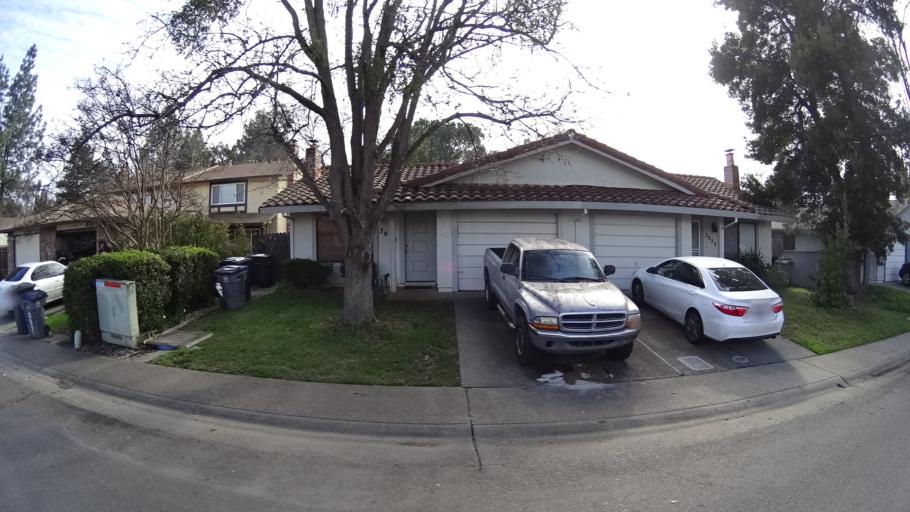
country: US
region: California
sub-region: Yolo County
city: Davis
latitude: 38.5462
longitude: -121.7141
